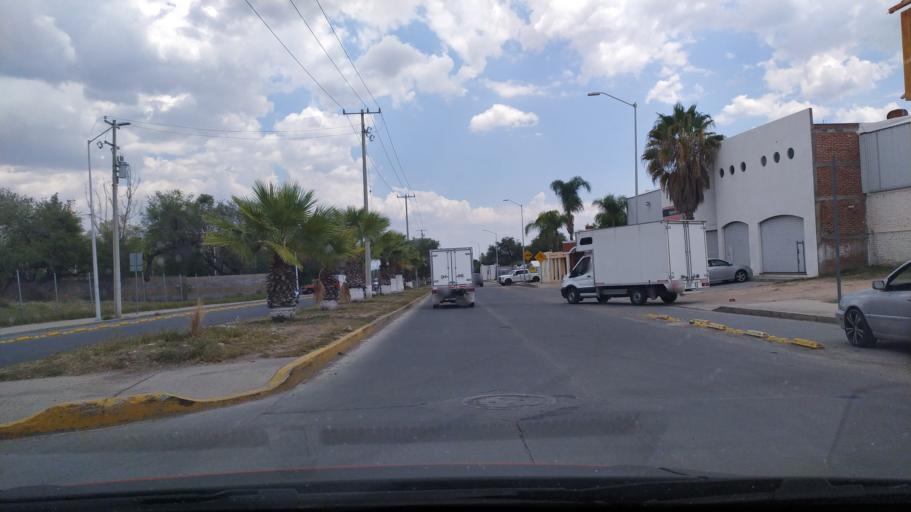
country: MX
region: Guanajuato
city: San Francisco del Rincon
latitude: 21.0382
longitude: -101.8696
